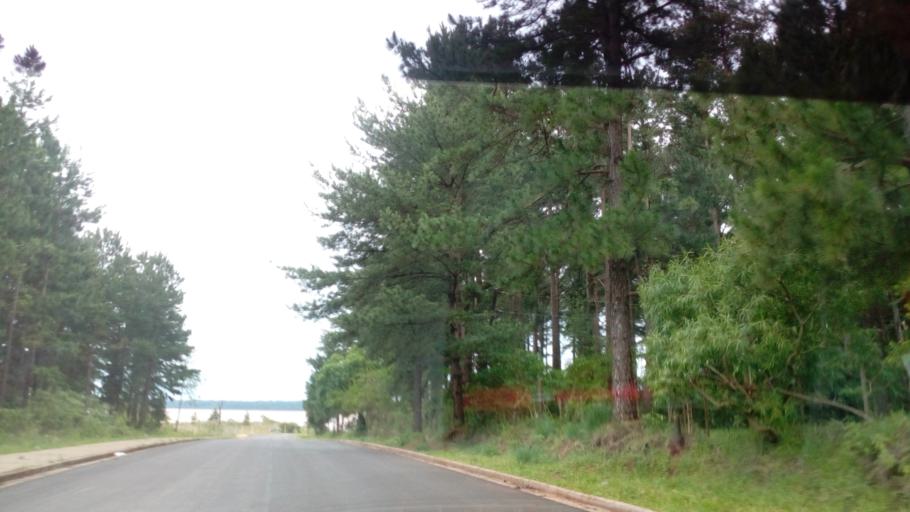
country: AR
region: Misiones
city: Garupa
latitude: -27.4579
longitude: -55.7917
